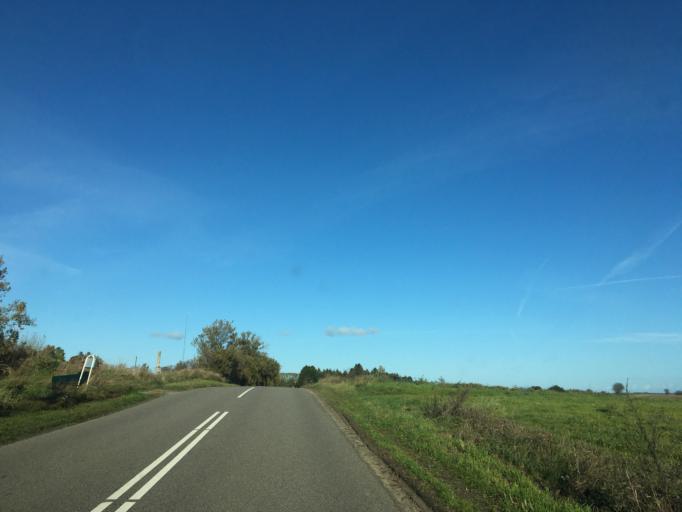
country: DK
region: Zealand
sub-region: Odsherred Kommune
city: Asnaes
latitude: 55.8385
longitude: 11.5566
